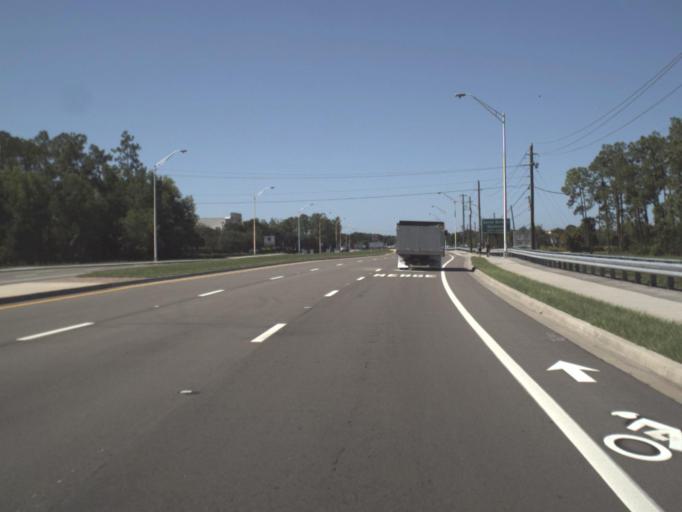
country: US
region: Florida
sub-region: Collier County
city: Lely
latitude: 26.1391
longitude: -81.7124
